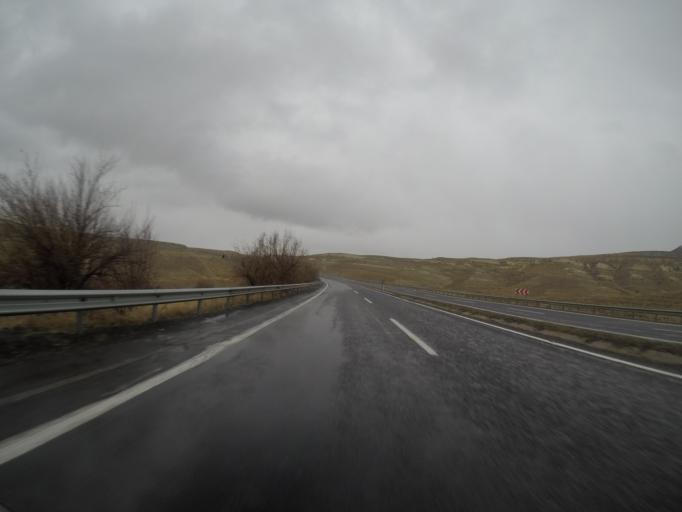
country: TR
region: Nevsehir
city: Urgub
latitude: 38.7389
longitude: 34.9958
